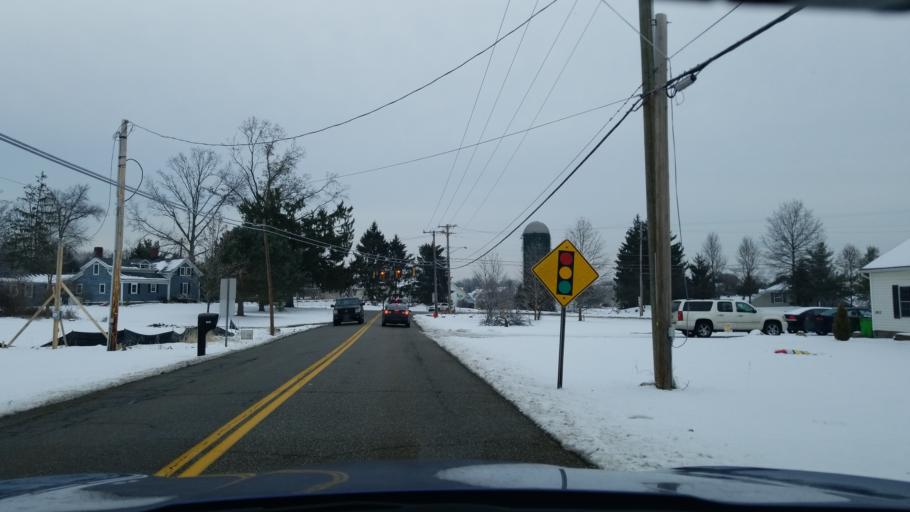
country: US
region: Ohio
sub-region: Summit County
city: Northfield
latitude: 41.3304
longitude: -81.5539
